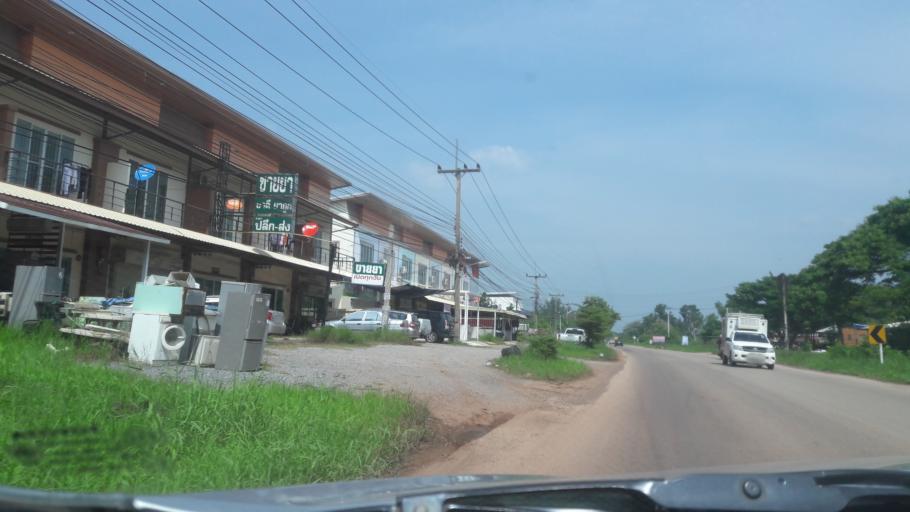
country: TH
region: Changwat Udon Thani
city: Udon Thani
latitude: 17.4343
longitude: 102.8319
